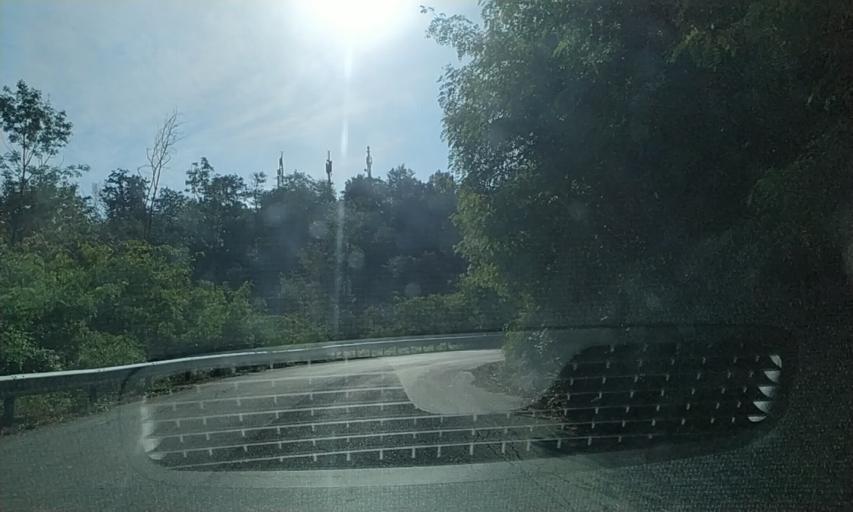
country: IT
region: Piedmont
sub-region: Provincia di Biella
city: Coggiola
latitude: 45.6813
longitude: 8.1840
